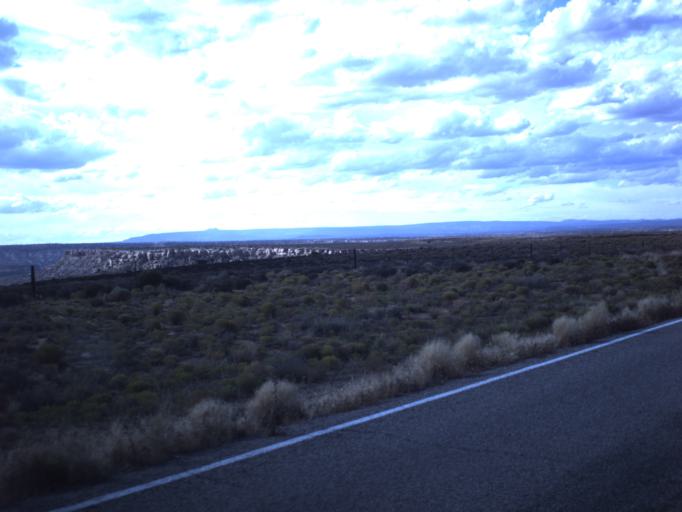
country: US
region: Utah
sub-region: San Juan County
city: Blanding
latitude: 37.3393
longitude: -109.3491
